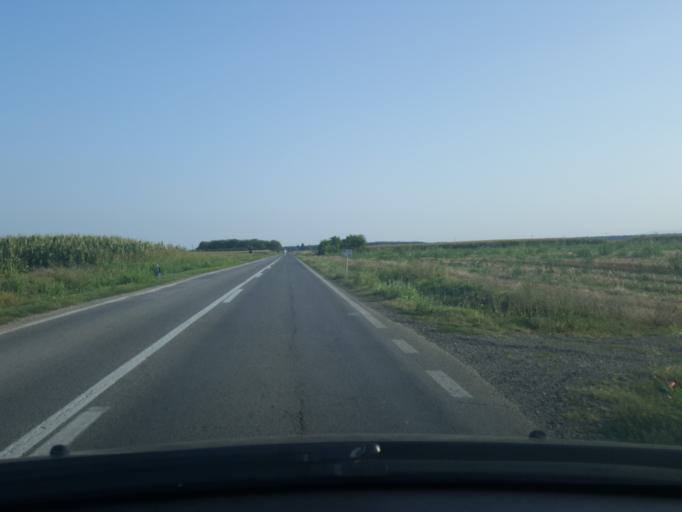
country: RS
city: Hrtkovci
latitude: 44.8615
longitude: 19.7717
